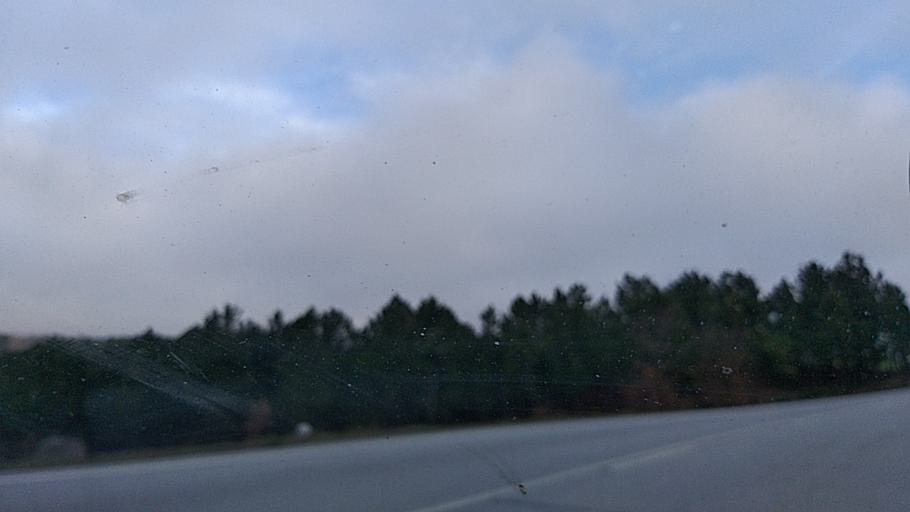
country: PT
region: Guarda
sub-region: Fornos de Algodres
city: Fornos de Algodres
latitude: 40.6692
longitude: -7.4753
